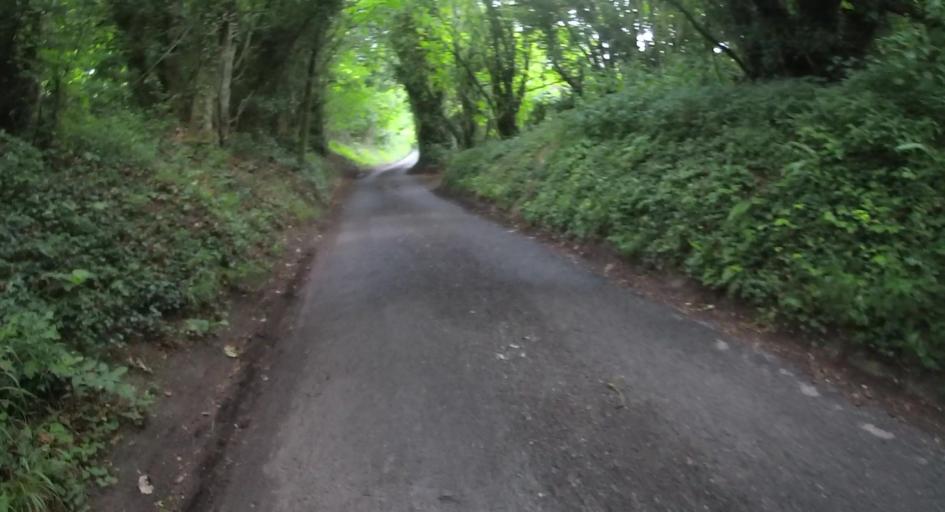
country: GB
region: England
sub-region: Hampshire
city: Long Sutton
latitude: 51.1993
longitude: -0.9143
